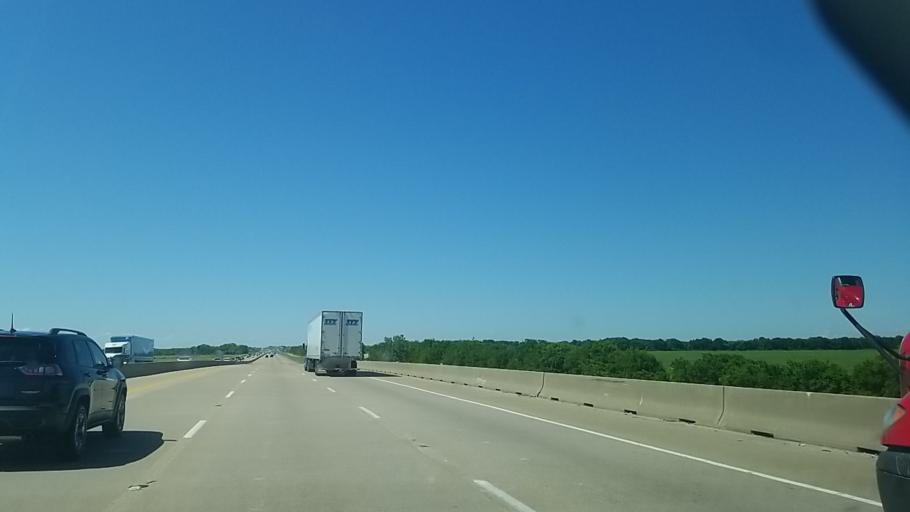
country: US
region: Texas
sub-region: Navarro County
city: Corsicana
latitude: 32.1645
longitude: -96.4692
